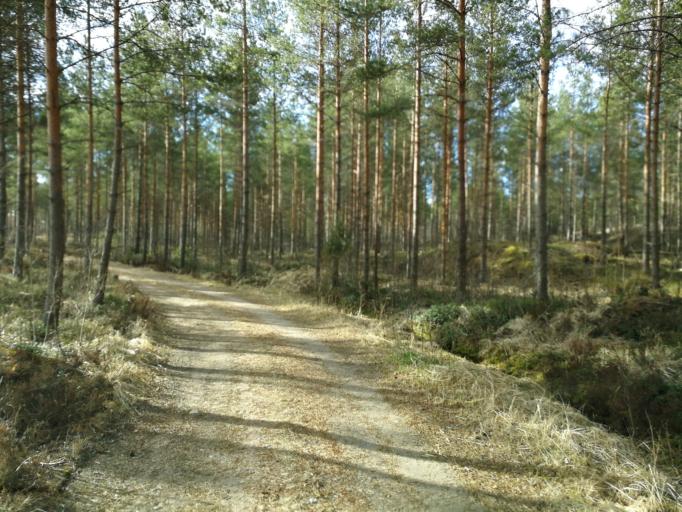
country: FI
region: Uusimaa
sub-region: Helsinki
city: Karjalohja
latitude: 60.2120
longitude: 23.6648
